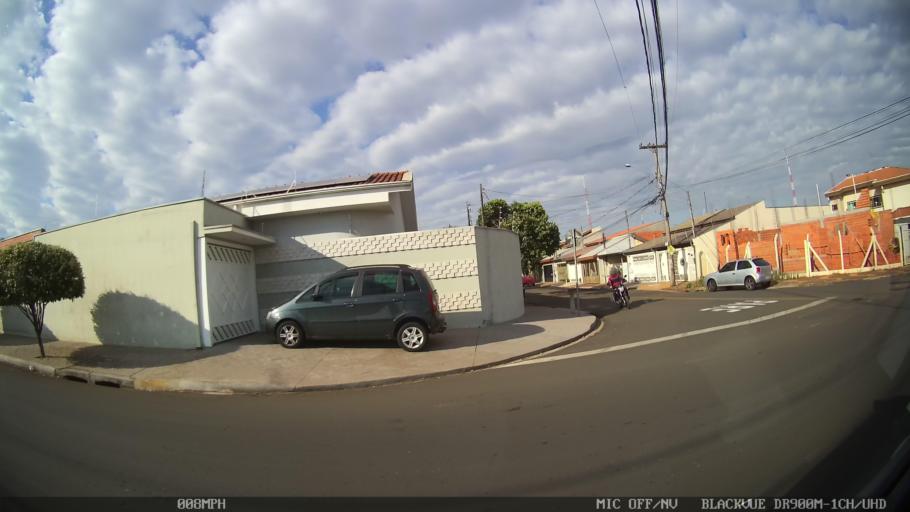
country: BR
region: Sao Paulo
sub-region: Americana
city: Americana
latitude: -22.7334
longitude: -47.3607
